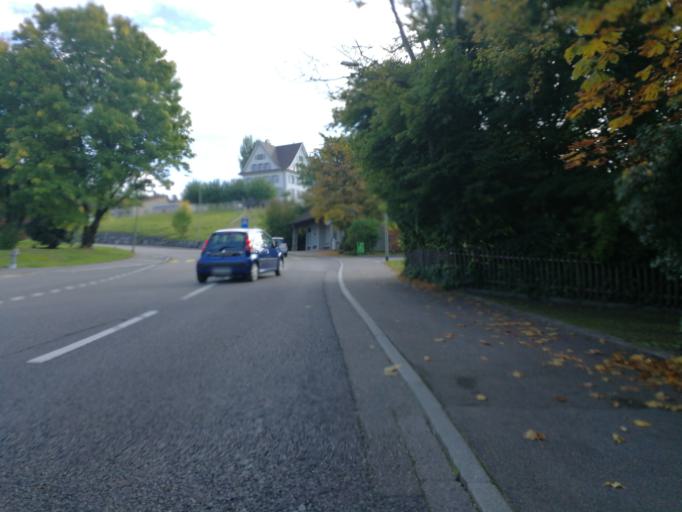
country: CH
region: Zurich
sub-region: Bezirk Meilen
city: Mannedorf
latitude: 47.2534
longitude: 8.7014
